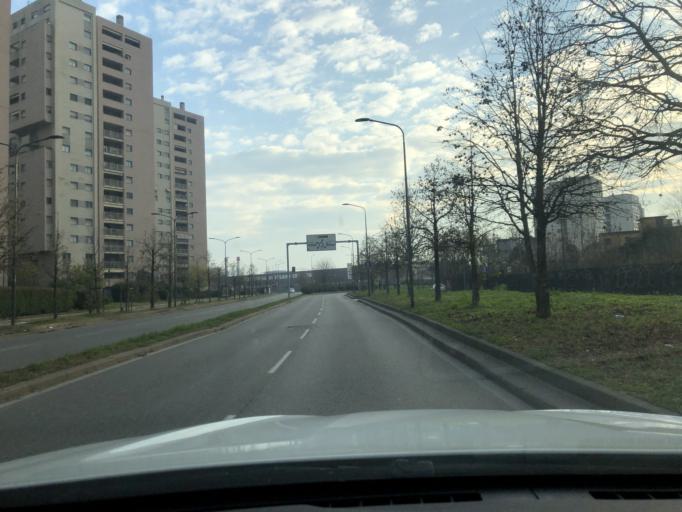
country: IT
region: Lombardy
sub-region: Citta metropolitana di Milano
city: Novate Milanese
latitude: 45.5096
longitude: 9.1378
